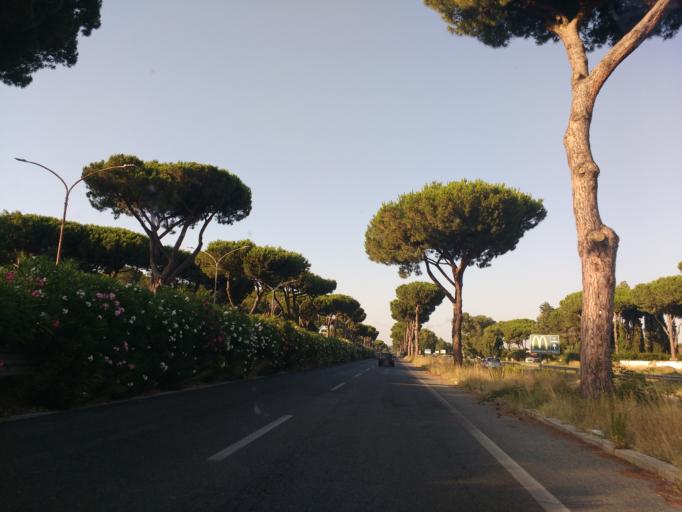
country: IT
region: Latium
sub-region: Citta metropolitana di Roma Capitale
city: Acilia-Castel Fusano-Ostia Antica
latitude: 41.7423
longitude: 12.3534
